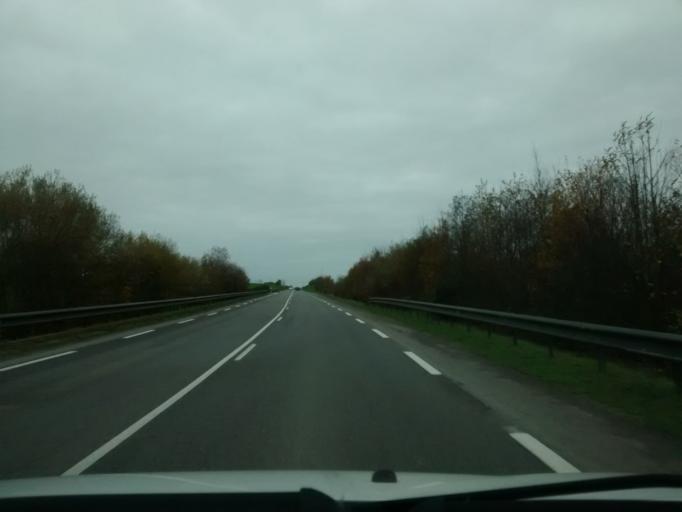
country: FR
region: Brittany
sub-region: Departement d'Ille-et-Vilaine
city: Etrelles
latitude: 48.0658
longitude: -1.1713
